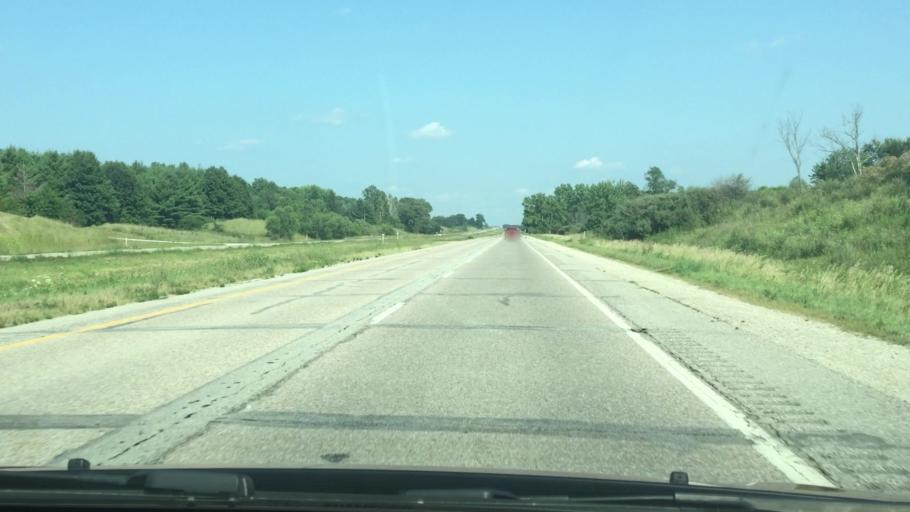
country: US
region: Iowa
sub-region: Scott County
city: Blue Grass
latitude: 41.5161
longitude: -90.8322
